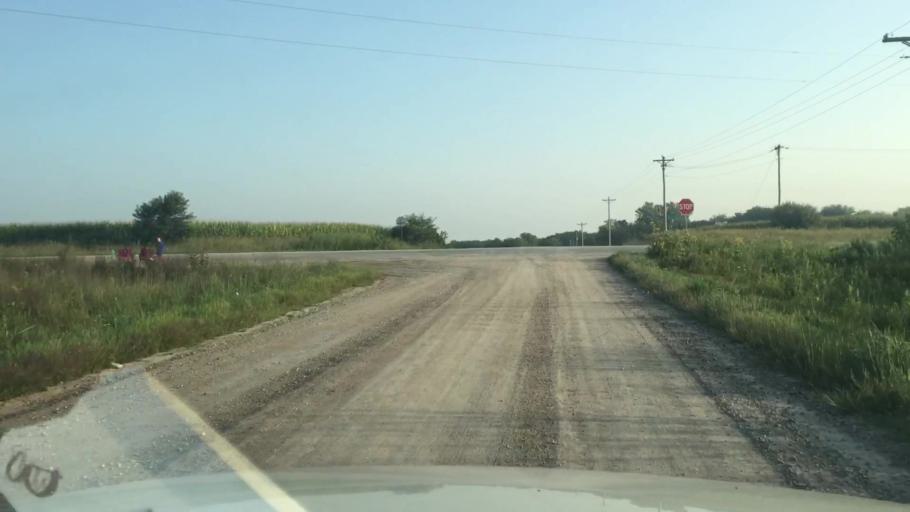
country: US
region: Iowa
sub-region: Story County
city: Huxley
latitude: 41.8988
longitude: -93.5809
